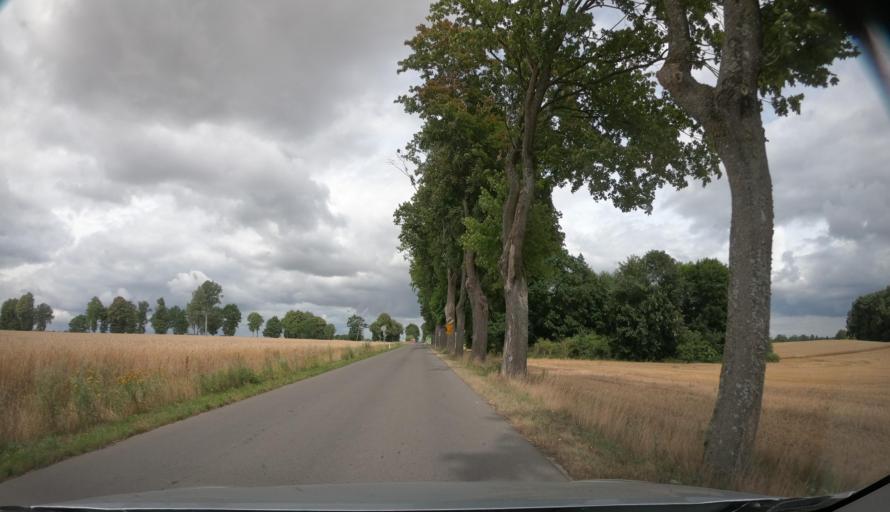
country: PL
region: West Pomeranian Voivodeship
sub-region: Koszalin
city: Koszalin
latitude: 54.1529
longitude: 16.0808
